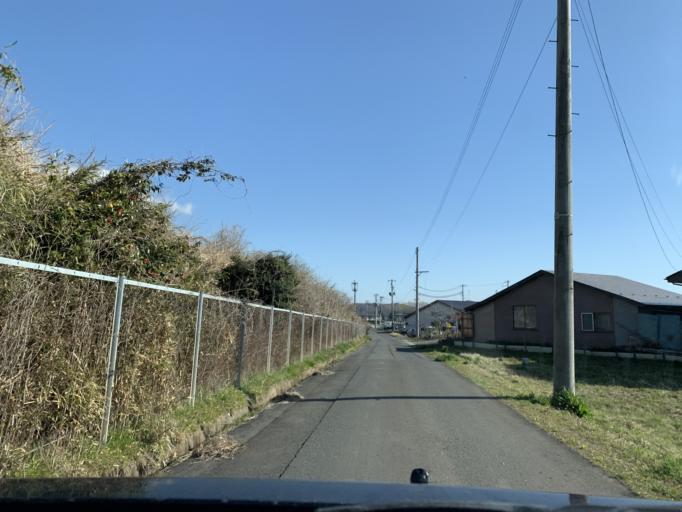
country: JP
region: Iwate
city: Ichinoseki
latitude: 38.9187
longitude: 141.1023
